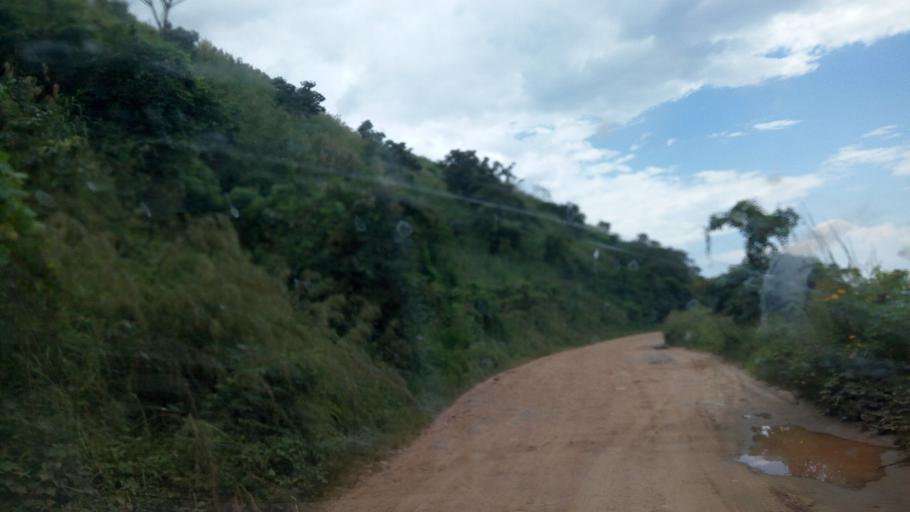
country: CD
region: South Kivu
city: Uvira
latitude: -3.5276
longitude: 29.1495
